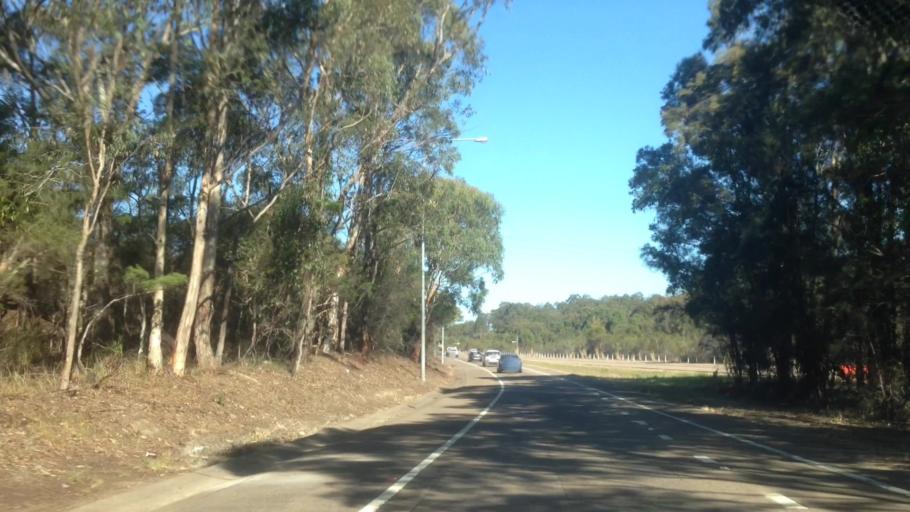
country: AU
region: New South Wales
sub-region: Lake Macquarie Shire
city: Cooranbong
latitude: -33.1200
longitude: 151.4670
